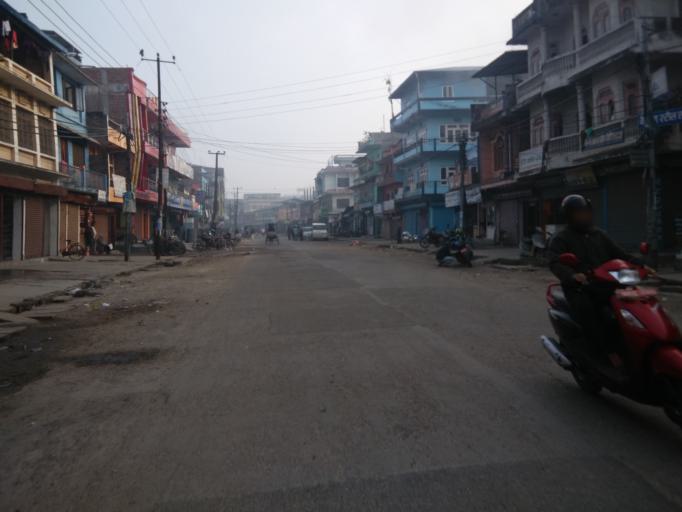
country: NP
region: Central Region
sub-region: Narayani Zone
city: Bharatpur
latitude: 27.6917
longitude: 84.4212
